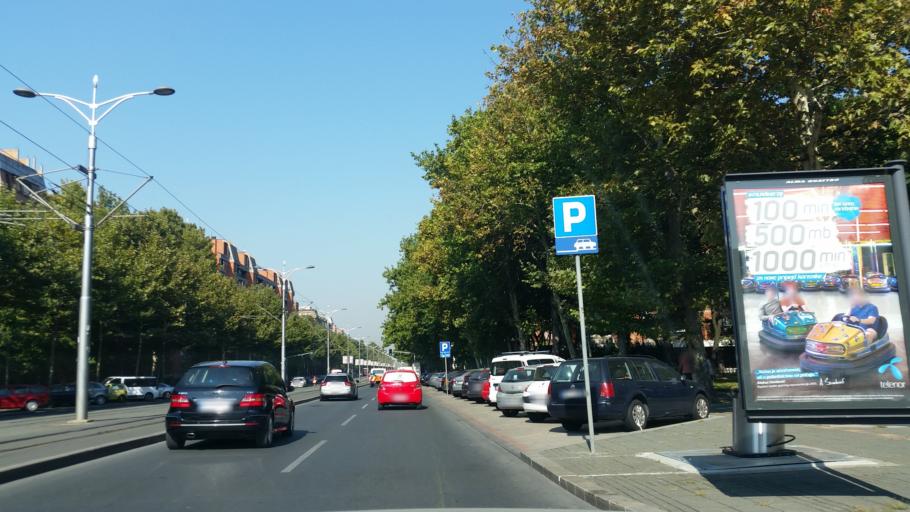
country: RS
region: Central Serbia
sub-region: Belgrade
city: Palilula
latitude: 44.7938
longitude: 20.5035
